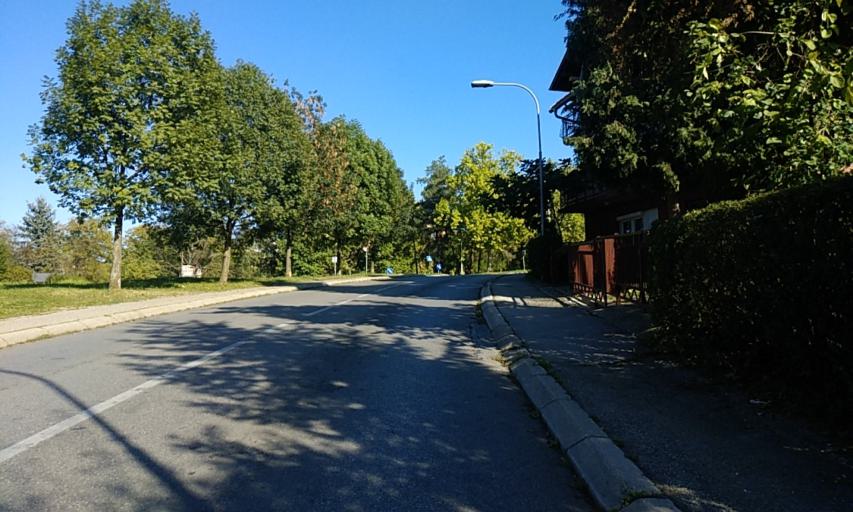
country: BA
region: Republika Srpska
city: Starcevica
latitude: 44.7594
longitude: 17.2031
